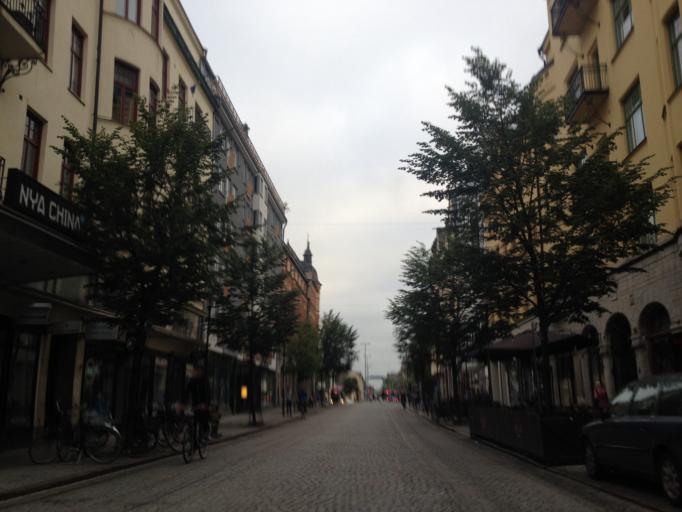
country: SE
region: OErebro
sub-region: Orebro Kommun
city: Orebro
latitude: 59.2766
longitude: 15.2156
